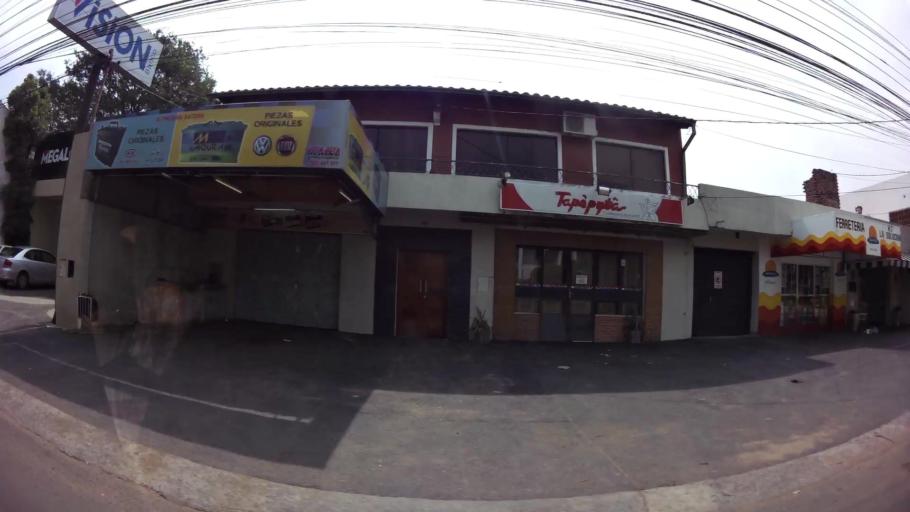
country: PY
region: Asuncion
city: Asuncion
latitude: -25.2725
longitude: -57.5655
